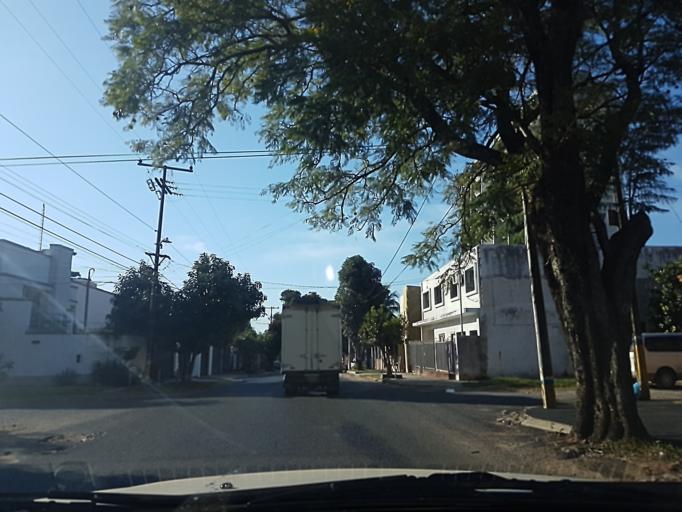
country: PY
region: Asuncion
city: Asuncion
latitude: -25.2614
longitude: -57.5647
